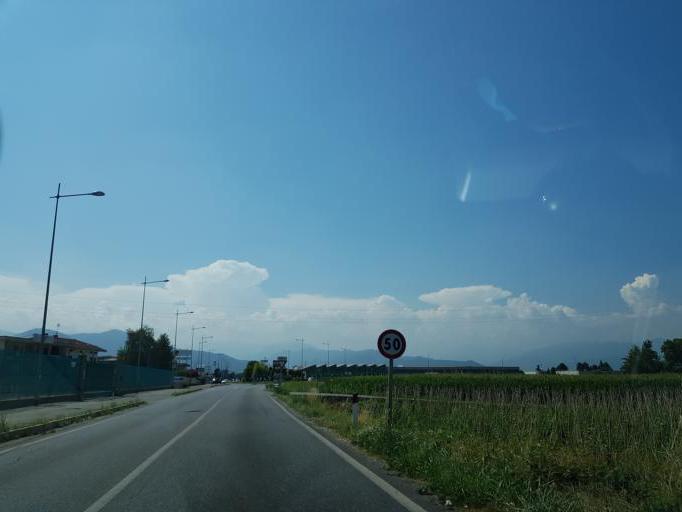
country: IT
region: Piedmont
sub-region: Provincia di Cuneo
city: San Defendente
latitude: 44.3950
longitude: 7.4996
